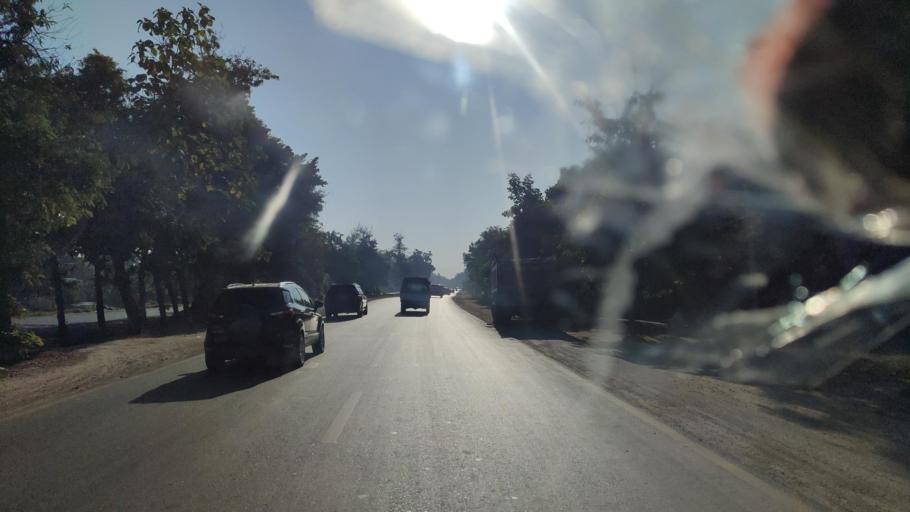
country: MM
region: Mandalay
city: Mandalay
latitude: 21.9179
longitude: 96.1641
